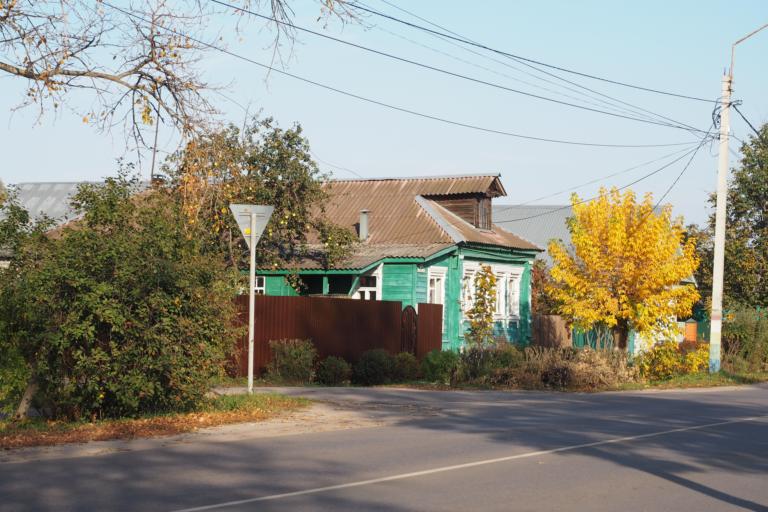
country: RU
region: Moskovskaya
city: Kurovskoye
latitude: 55.5793
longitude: 38.9246
